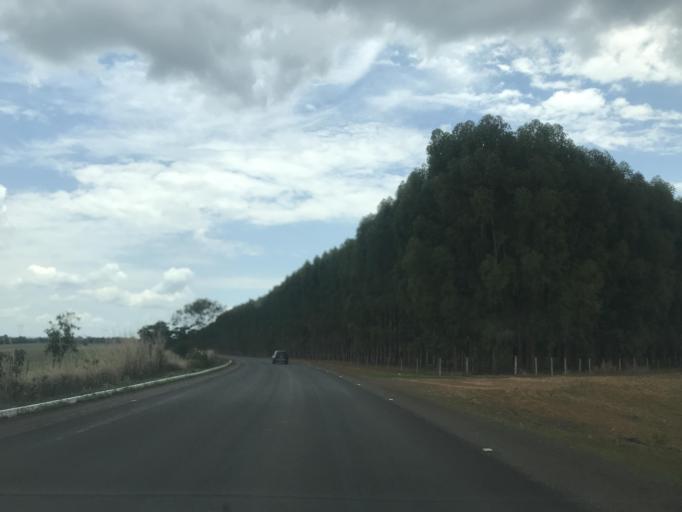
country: BR
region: Goias
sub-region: Vianopolis
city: Vianopolis
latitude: -16.9259
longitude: -48.5579
